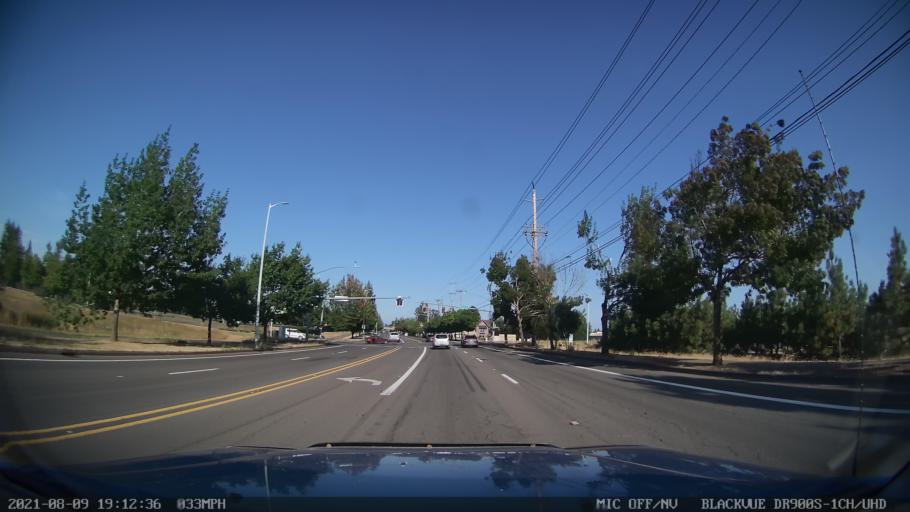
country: US
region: Oregon
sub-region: Marion County
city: Four Corners
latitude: 44.9280
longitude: -122.9997
